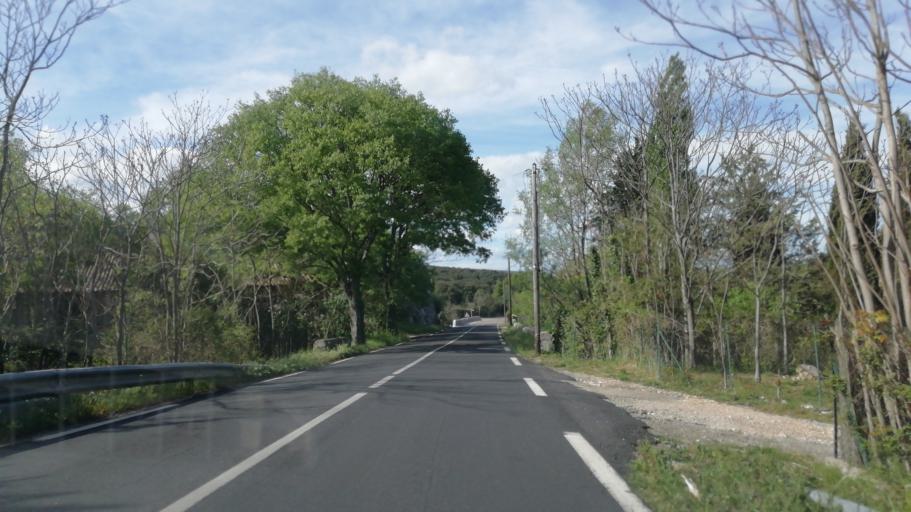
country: FR
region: Languedoc-Roussillon
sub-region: Departement de l'Herault
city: Saint-Martin-de-Londres
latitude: 43.7732
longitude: 3.7206
